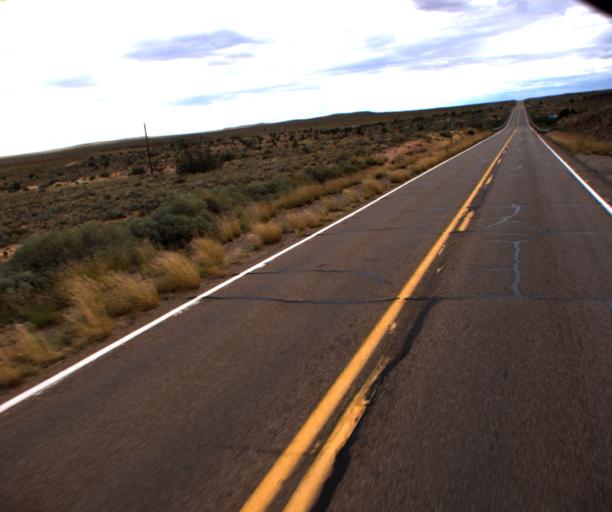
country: US
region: Arizona
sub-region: Navajo County
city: Holbrook
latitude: 34.8402
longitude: -110.1460
